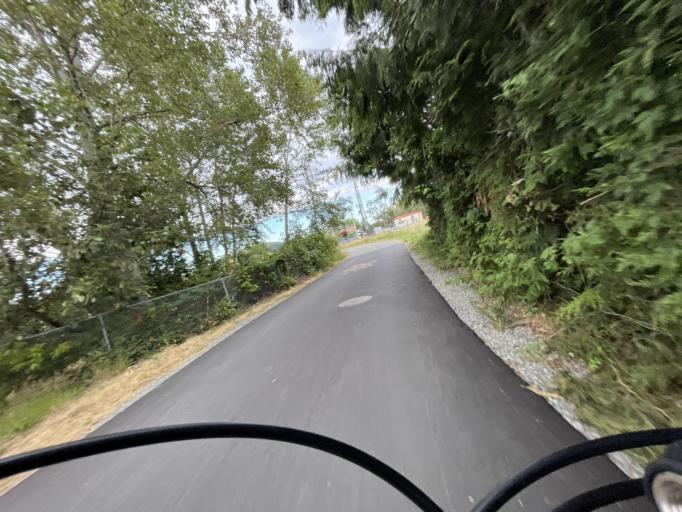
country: CA
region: British Columbia
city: Victoria
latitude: 48.4730
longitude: -123.3599
